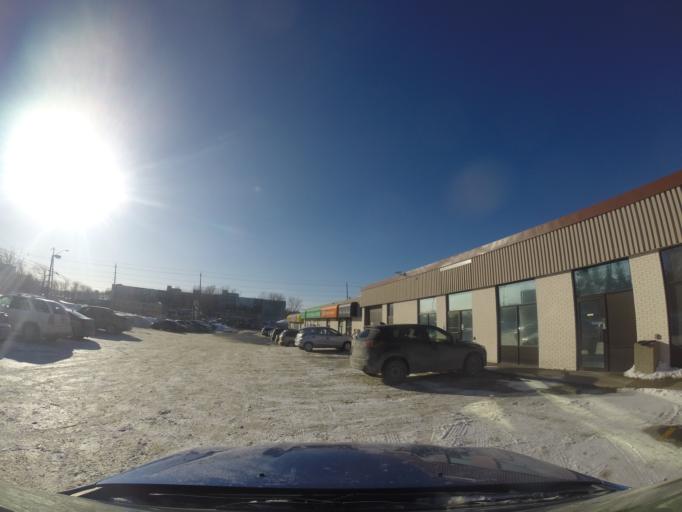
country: CA
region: Ontario
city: Greater Sudbury
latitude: 46.4619
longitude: -80.9991
